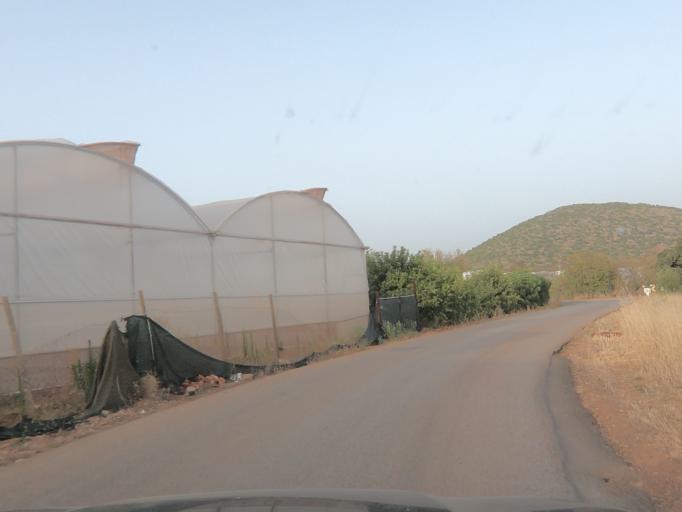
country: PT
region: Faro
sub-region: Loule
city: Vilamoura
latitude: 37.1143
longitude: -8.0828
